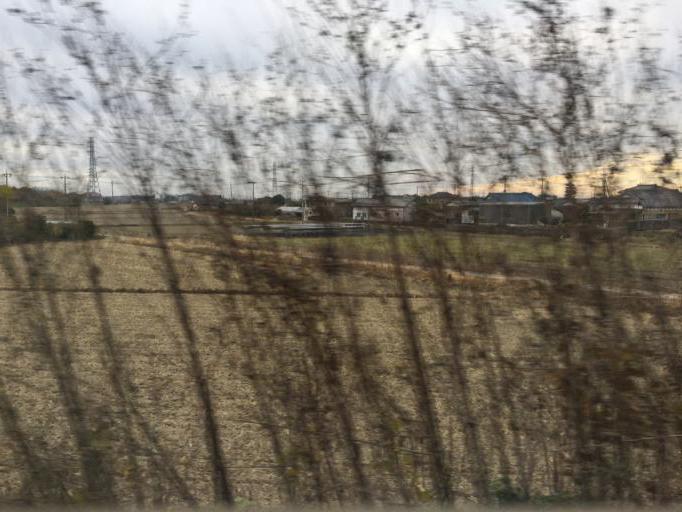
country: JP
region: Tochigi
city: Oyama
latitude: 36.3413
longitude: 139.8001
